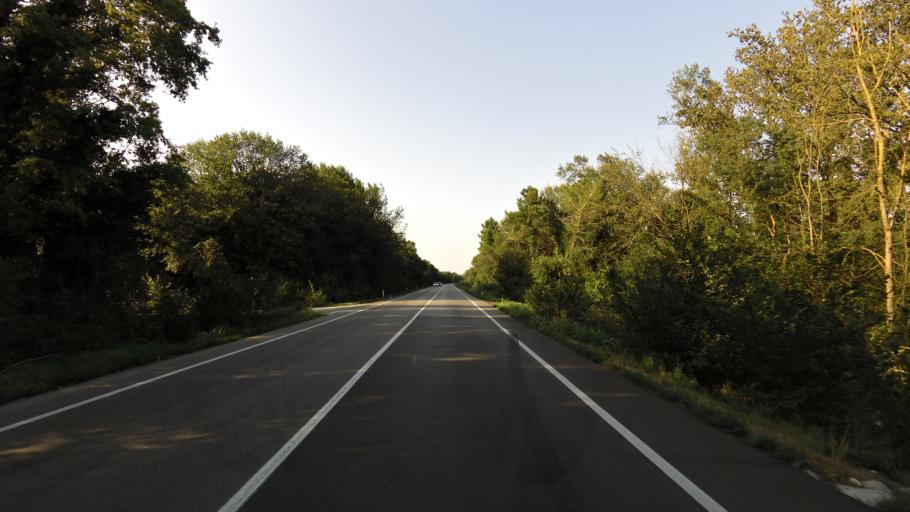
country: IT
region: Emilia-Romagna
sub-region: Provincia di Ravenna
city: Marina Romea
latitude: 44.4939
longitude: 12.2158
